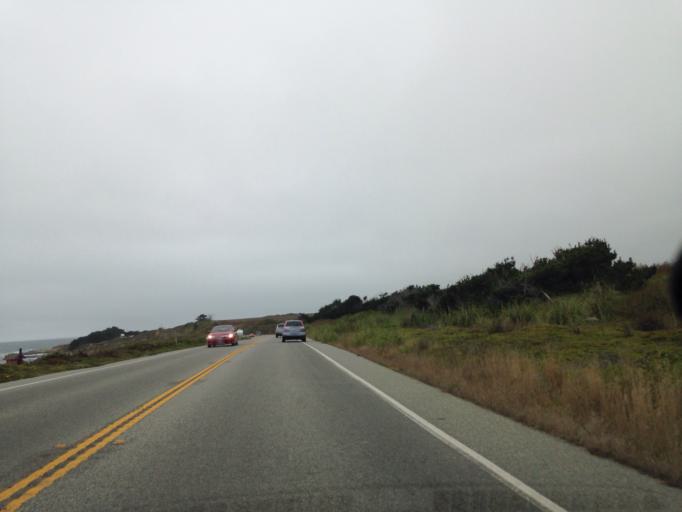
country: US
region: California
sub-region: San Mateo County
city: Half Moon Bay
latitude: 37.2349
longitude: -122.4151
